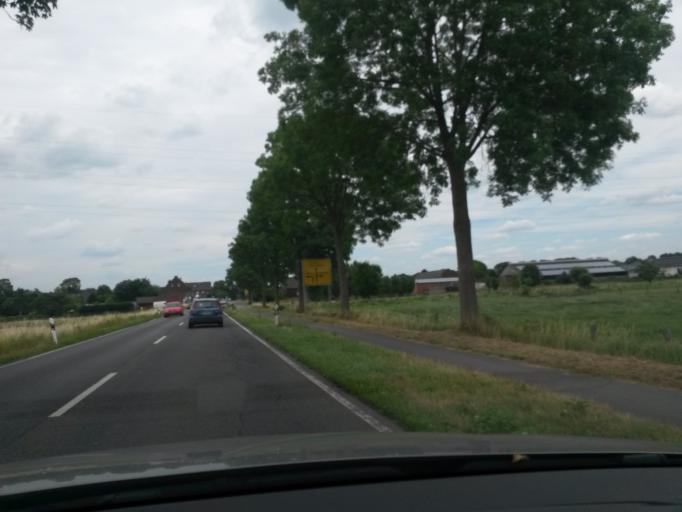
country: DE
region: North Rhine-Westphalia
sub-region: Regierungsbezirk Dusseldorf
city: Viersen
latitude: 51.2890
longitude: 6.3884
